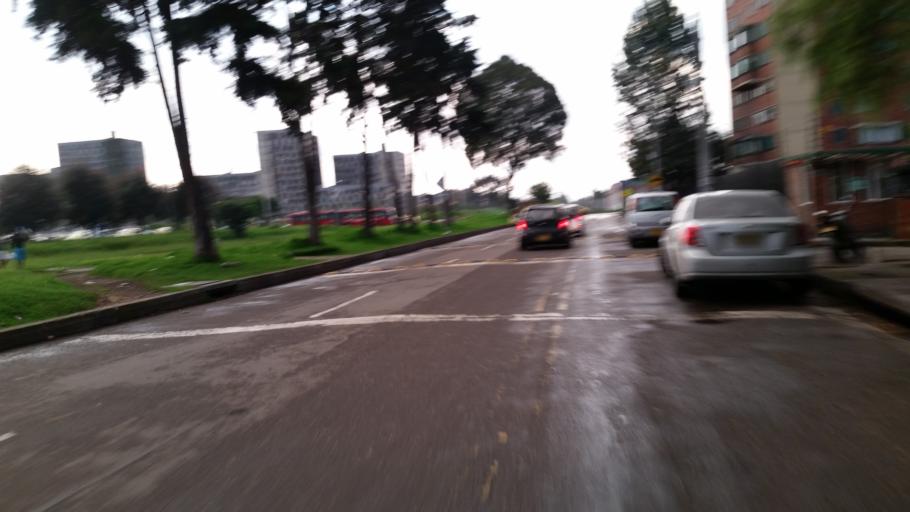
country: CO
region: Bogota D.C.
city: Bogota
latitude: 4.6199
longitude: -74.0856
